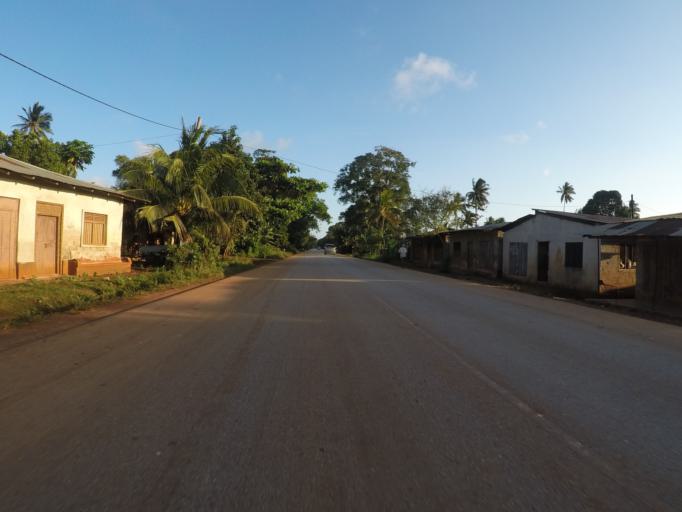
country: TZ
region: Zanzibar North
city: Mkokotoni
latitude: -5.8557
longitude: 39.2810
